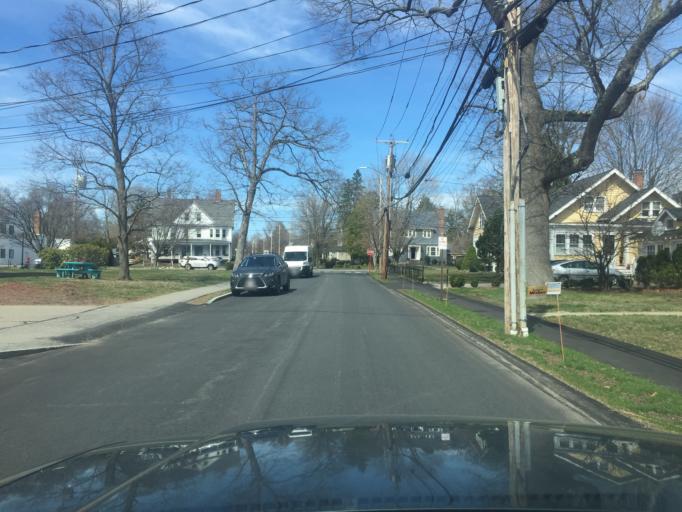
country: US
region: Massachusetts
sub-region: Norfolk County
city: Needham
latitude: 42.2796
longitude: -71.2329
